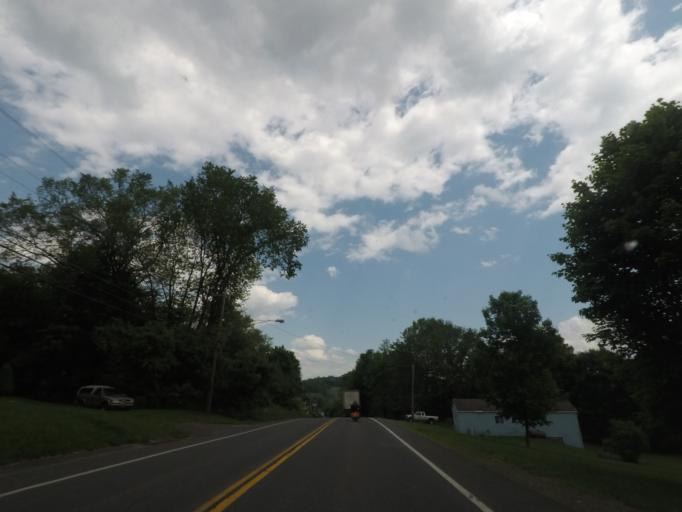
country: US
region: New York
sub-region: Dutchess County
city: Pine Plains
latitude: 42.0519
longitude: -73.6411
